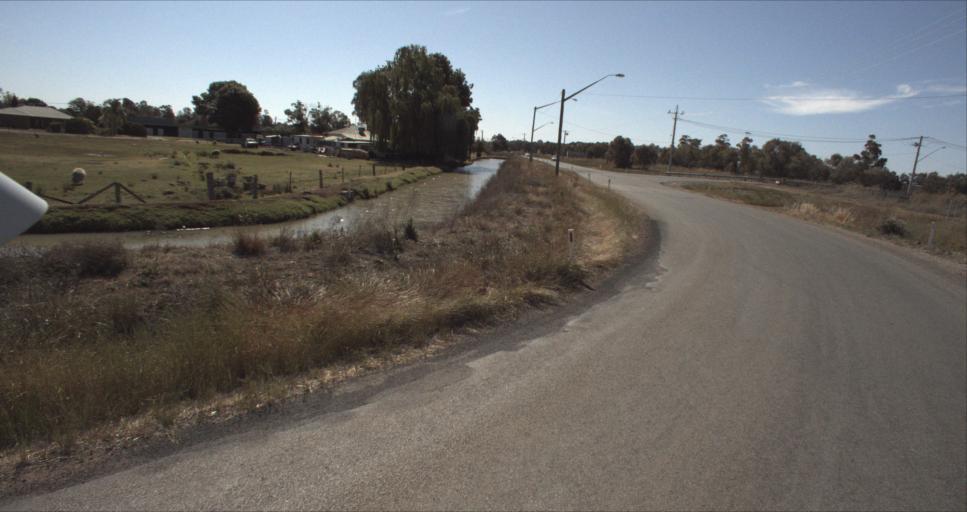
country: AU
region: New South Wales
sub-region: Leeton
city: Leeton
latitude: -34.5529
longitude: 146.3850
